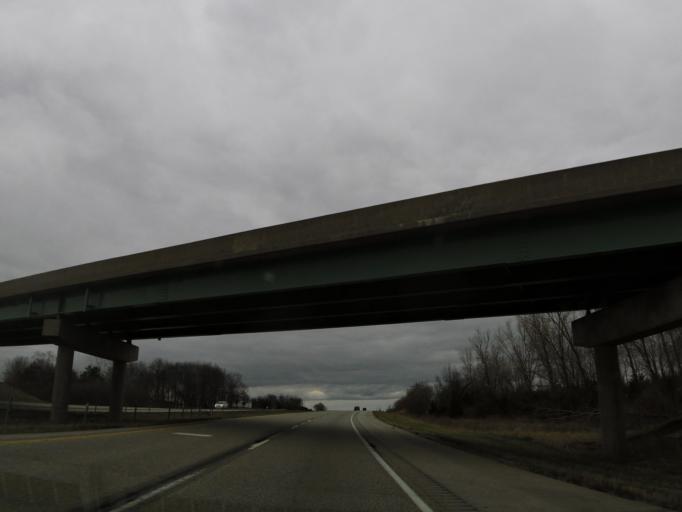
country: US
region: Iowa
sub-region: Linn County
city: Robins
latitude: 42.1251
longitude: -91.7174
